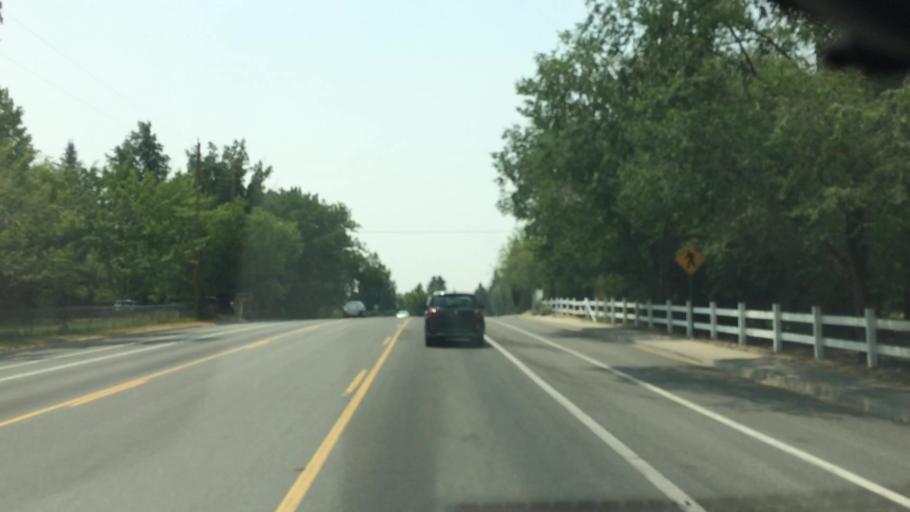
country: US
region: Nevada
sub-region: Washoe County
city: Reno
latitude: 39.4881
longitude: -119.8127
